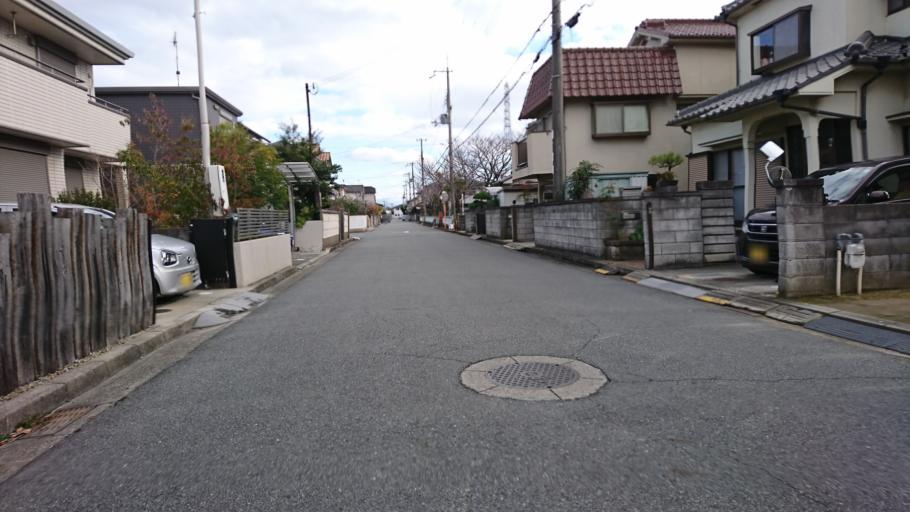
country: JP
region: Hyogo
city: Kakogawacho-honmachi
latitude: 34.7821
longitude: 134.8198
